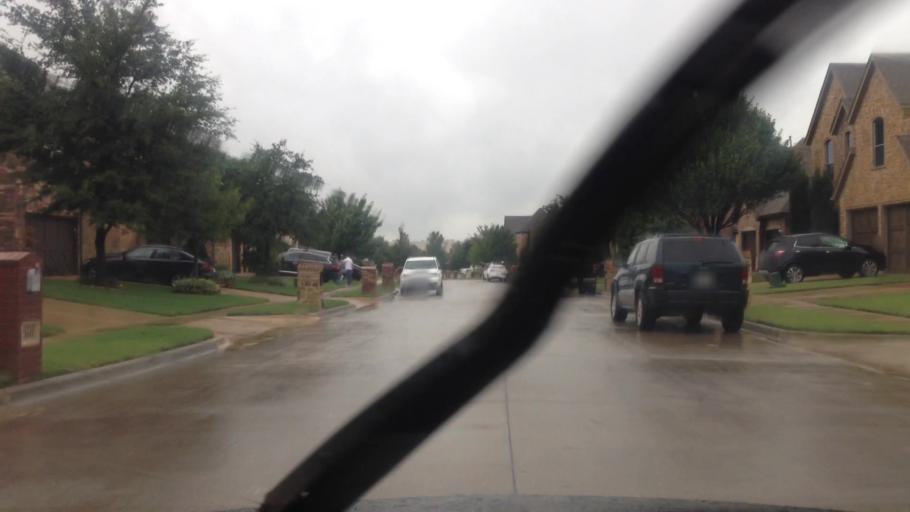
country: US
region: Texas
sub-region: Tarrant County
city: Watauga
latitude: 32.8934
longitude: -97.2411
